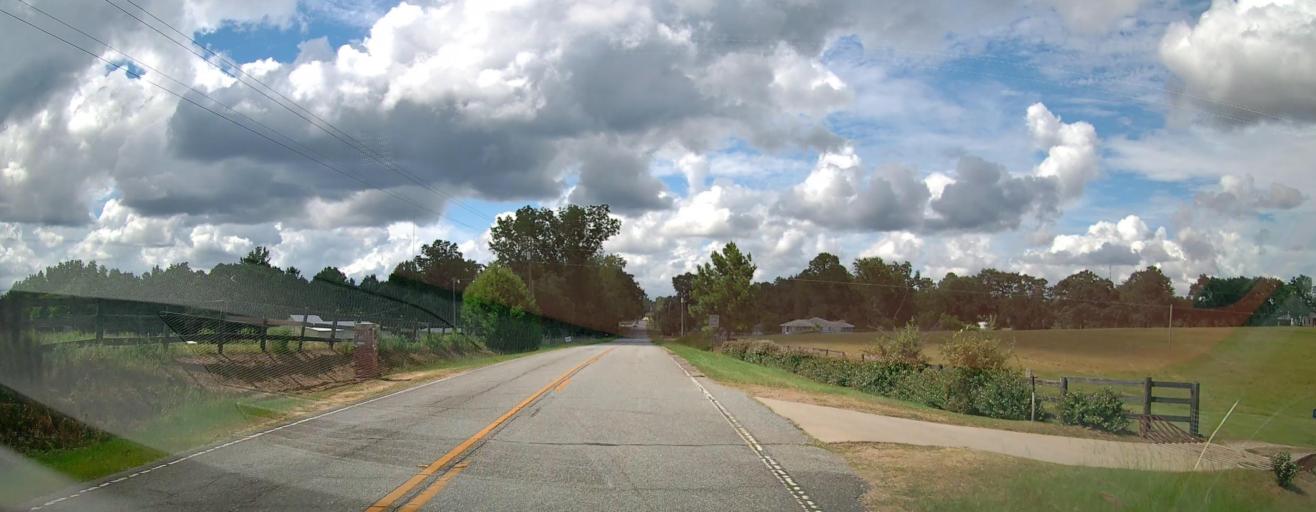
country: US
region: Georgia
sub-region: Chattahoochee County
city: Cusseta
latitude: 32.2951
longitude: -84.7687
